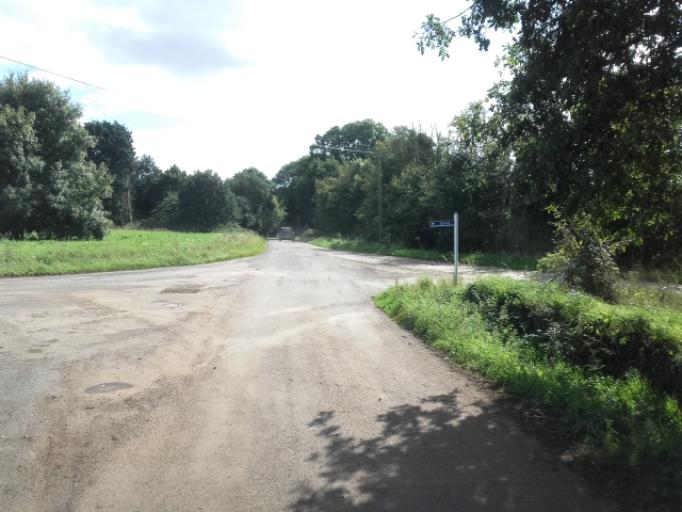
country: FR
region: Brittany
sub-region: Departement des Cotes-d'Armor
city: Lanvollon
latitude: 48.6106
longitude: -2.9715
